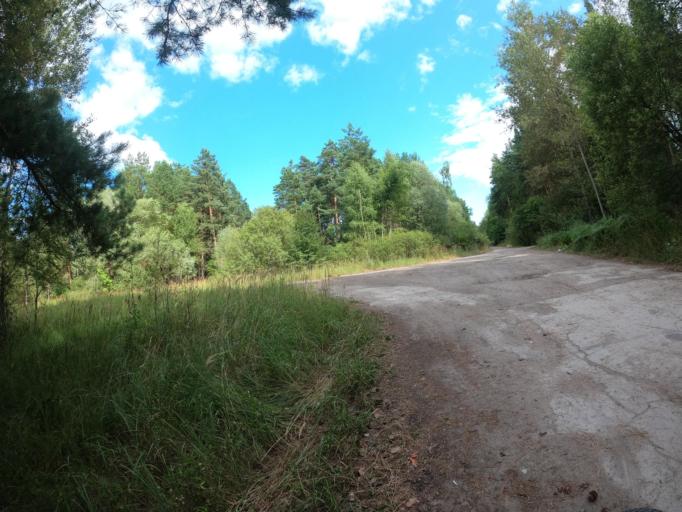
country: RU
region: Moskovskaya
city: Lopatinskiy
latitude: 55.3830
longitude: 38.7068
